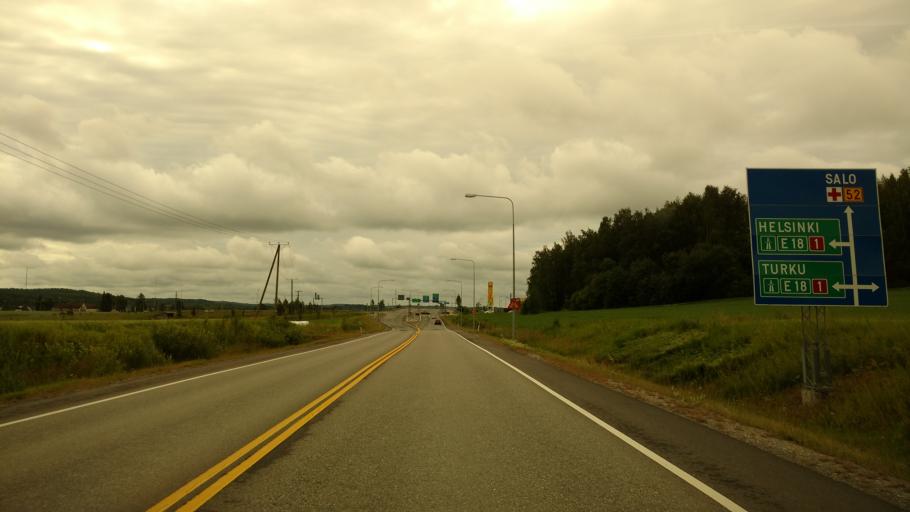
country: FI
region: Varsinais-Suomi
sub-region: Salo
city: Salo
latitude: 60.4221
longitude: 23.1683
